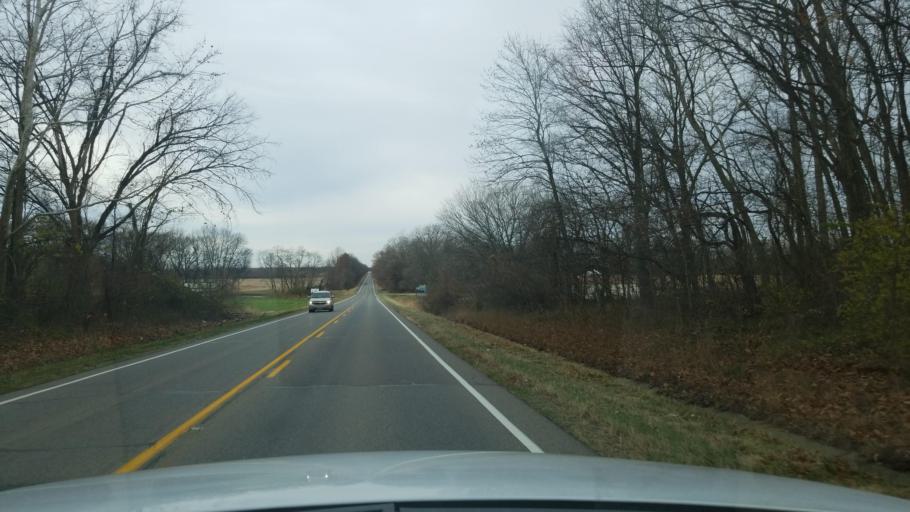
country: US
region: Indiana
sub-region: Posey County
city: Mount Vernon
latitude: 37.9290
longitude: -87.9598
